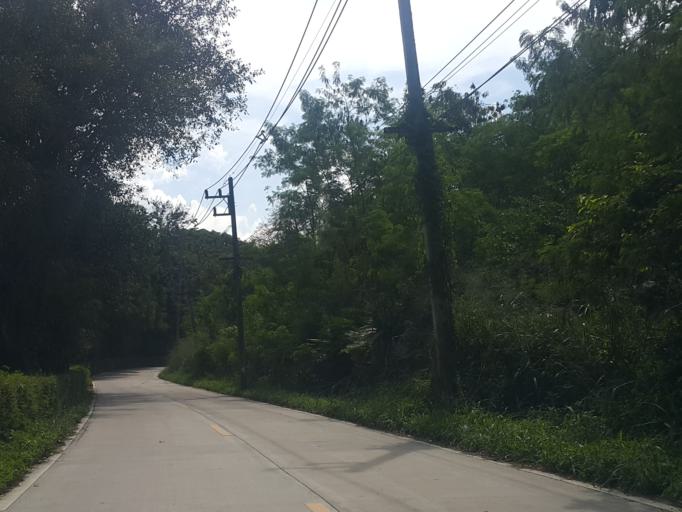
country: TH
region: Chiang Mai
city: Mae On
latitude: 18.8172
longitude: 99.2243
